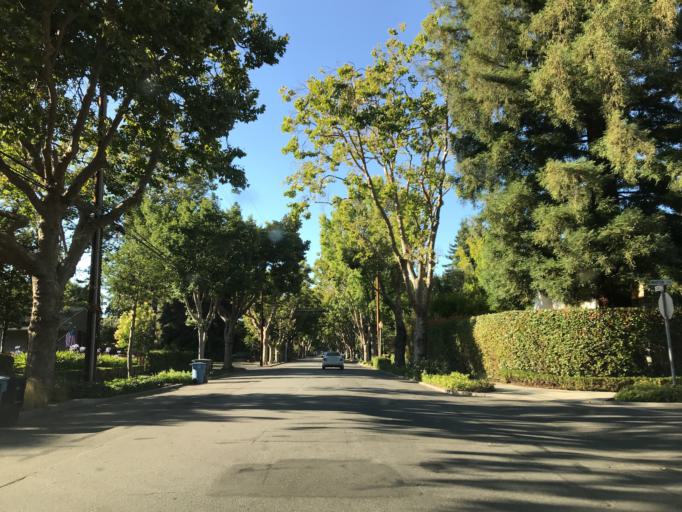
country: US
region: California
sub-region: Santa Clara County
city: Palo Alto
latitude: 37.4509
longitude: -122.1469
